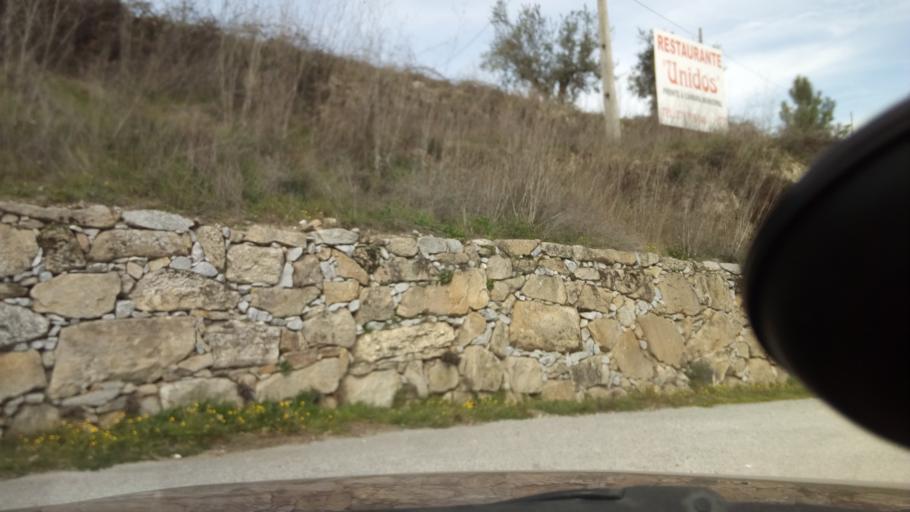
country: PT
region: Guarda
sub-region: Fornos de Algodres
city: Fornos de Algodres
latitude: 40.6133
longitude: -7.5382
